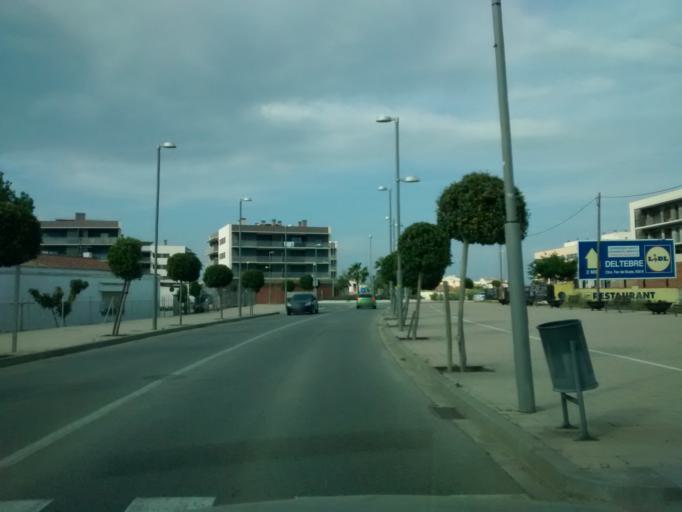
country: ES
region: Catalonia
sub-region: Provincia de Tarragona
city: Deltebre
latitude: 40.7149
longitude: 0.7182
